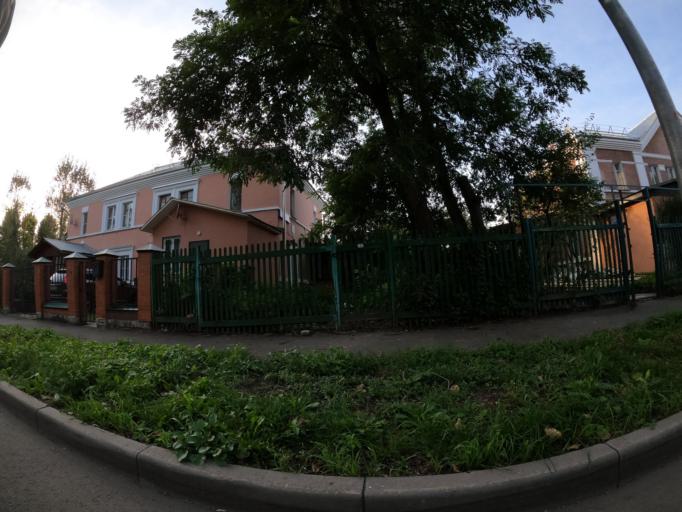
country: RU
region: Moskovskaya
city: Kur'yanovo
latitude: 55.6532
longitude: 37.6994
